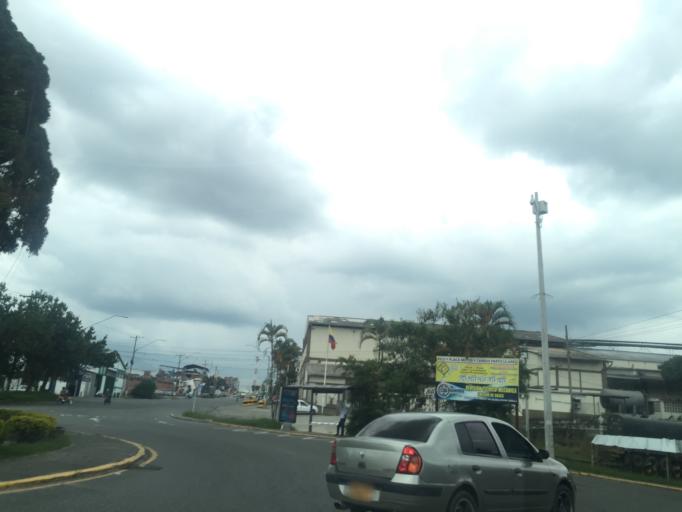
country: CO
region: Quindio
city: Armenia
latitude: 4.5177
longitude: -75.6908
